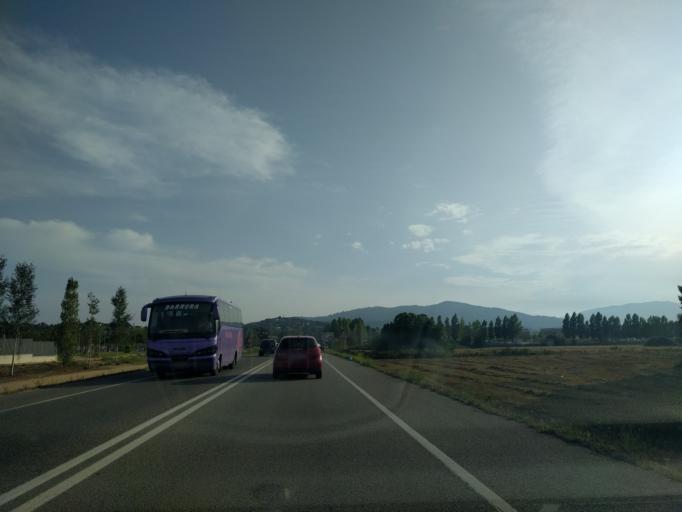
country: ES
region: Catalonia
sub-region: Provincia de Barcelona
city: Tordera
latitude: 41.6978
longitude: 2.7271
